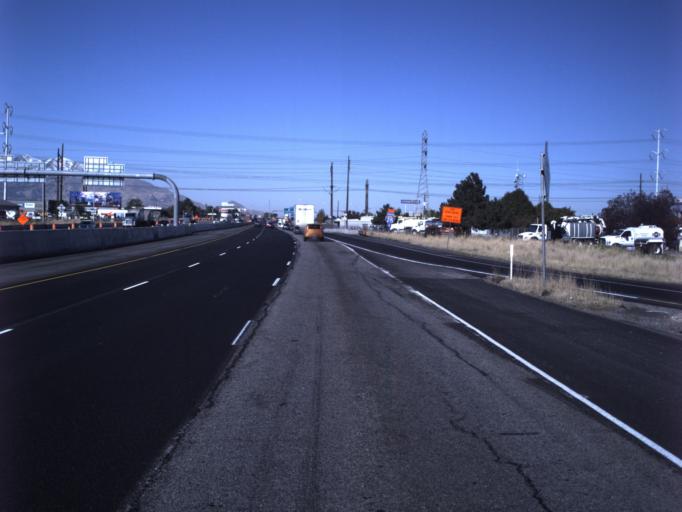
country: US
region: Utah
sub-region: Salt Lake County
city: West Valley City
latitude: 40.7259
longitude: -111.9555
